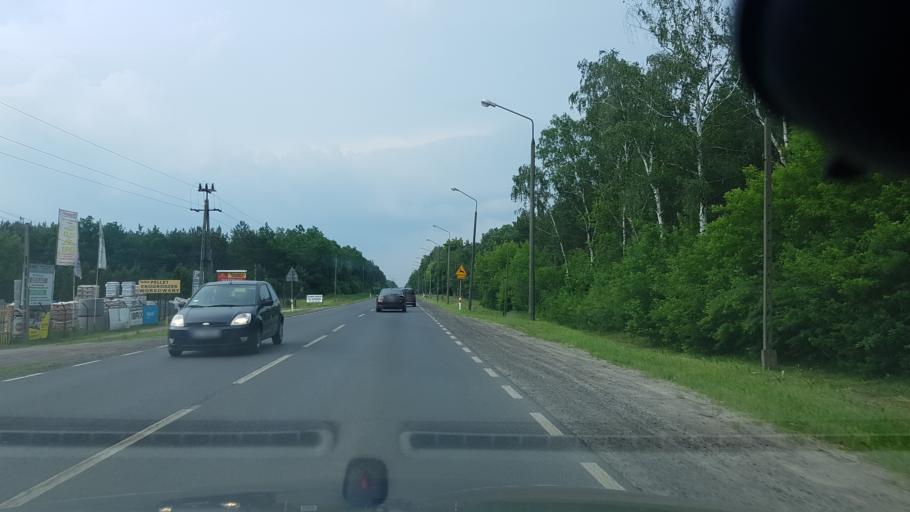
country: PL
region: Masovian Voivodeship
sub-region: Powiat legionowski
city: Michalow-Reginow
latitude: 52.4295
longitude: 20.9818
